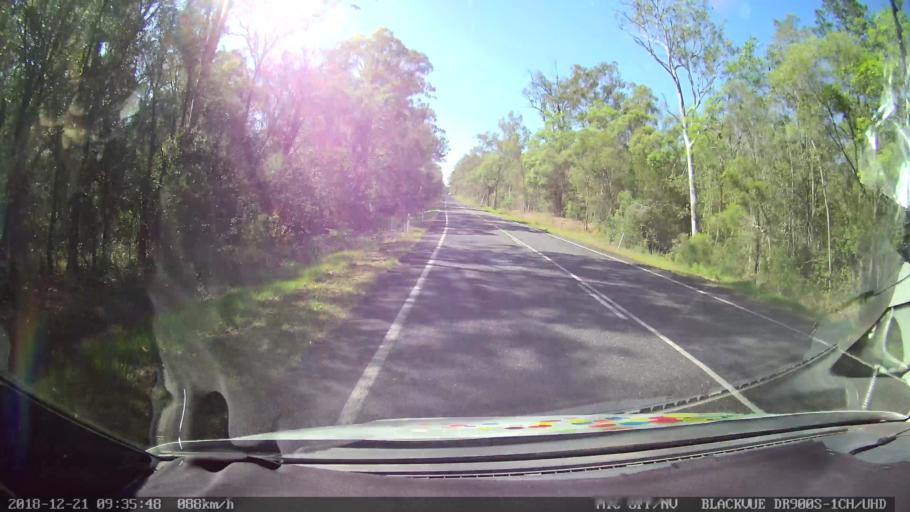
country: AU
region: New South Wales
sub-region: Clarence Valley
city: Grafton
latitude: -29.5154
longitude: 152.9805
